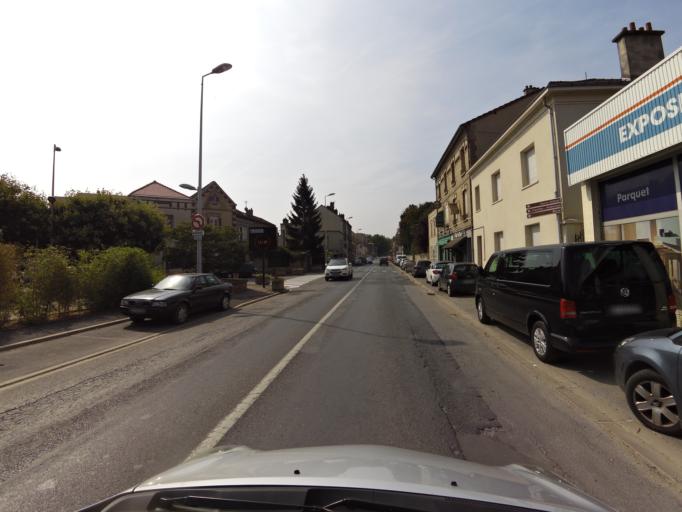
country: FR
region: Champagne-Ardenne
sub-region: Departement de la Marne
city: Magenta
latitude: 49.0491
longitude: 3.9650
